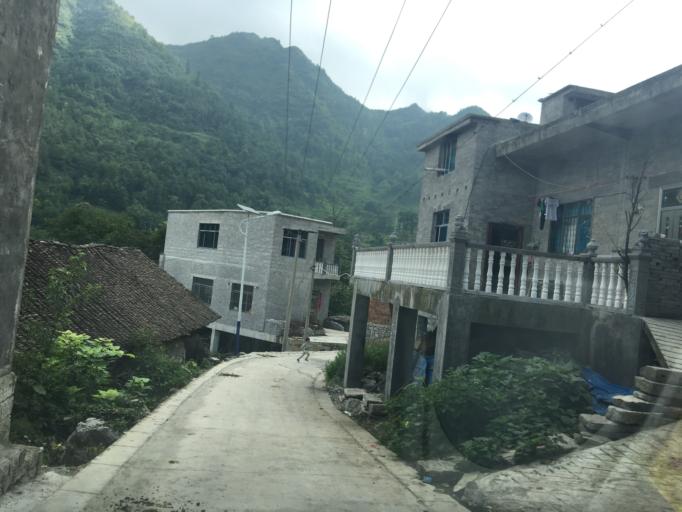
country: CN
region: Guangxi Zhuangzu Zizhiqu
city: Xinzhou
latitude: 25.0742
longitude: 105.7258
